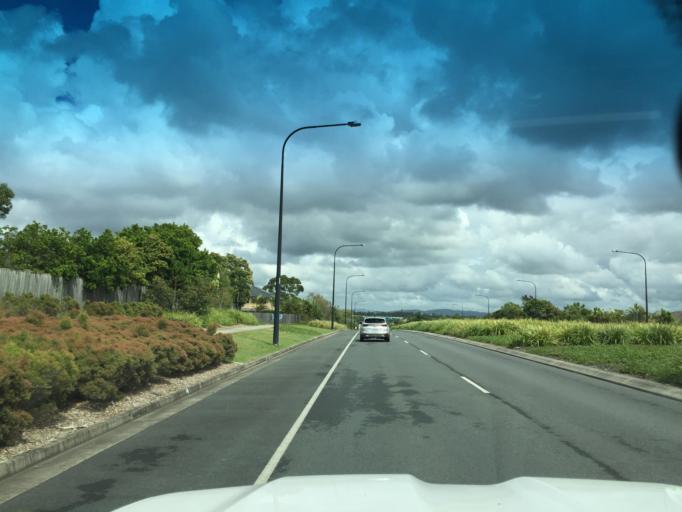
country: AU
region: Queensland
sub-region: Moreton Bay
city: Mango Hill
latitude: -27.2293
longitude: 153.0162
